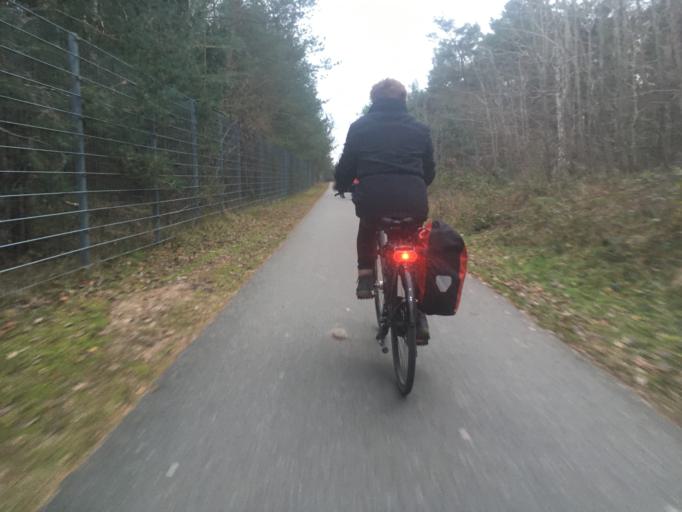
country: DE
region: Mecklenburg-Vorpommern
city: Sagard
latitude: 54.4601
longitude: 13.5666
